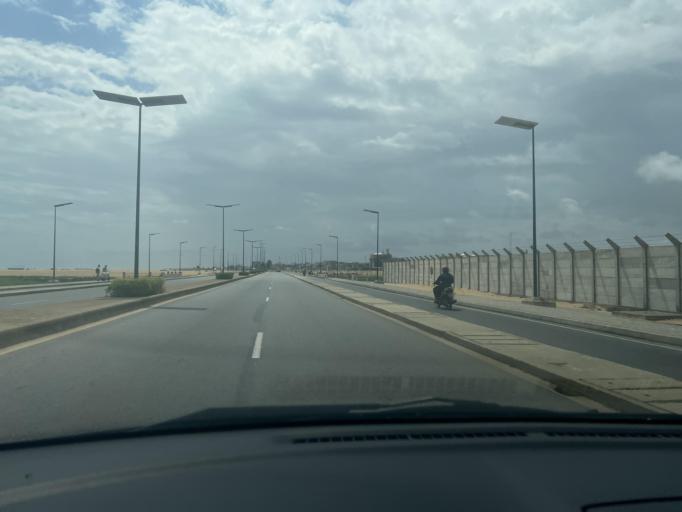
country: BJ
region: Littoral
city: Cotonou
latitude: 6.3484
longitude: 2.3741
